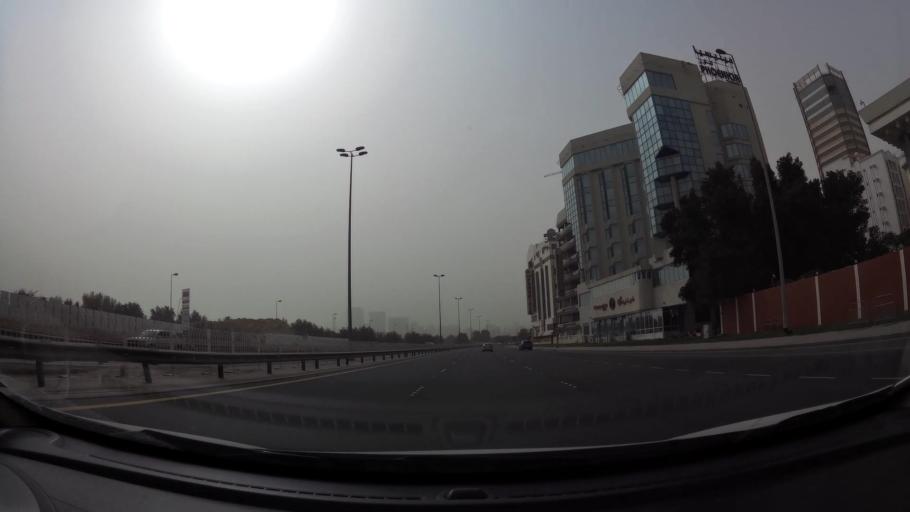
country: BH
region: Muharraq
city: Al Muharraq
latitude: 26.2374
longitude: 50.5967
